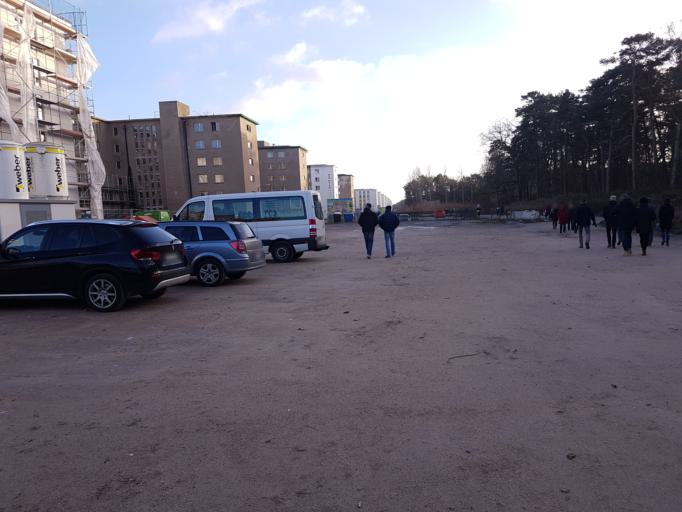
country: DE
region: Mecklenburg-Vorpommern
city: Ostseebad Binz
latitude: 54.4371
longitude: 13.5758
